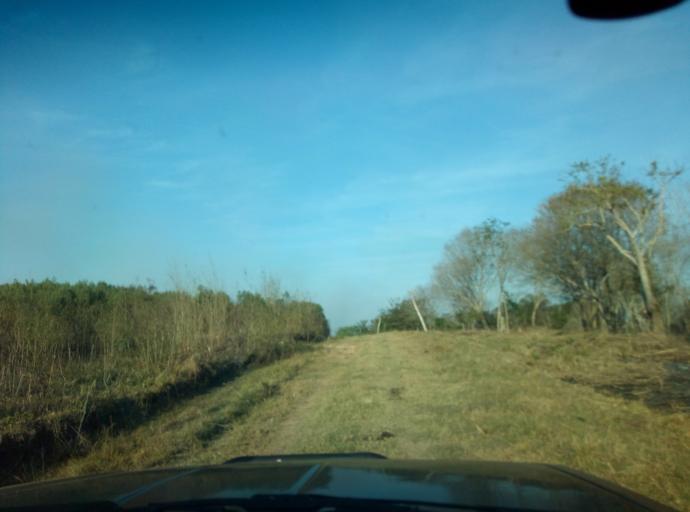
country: PY
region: Caaguazu
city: Doctor Cecilio Baez
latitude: -25.1999
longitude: -56.1229
